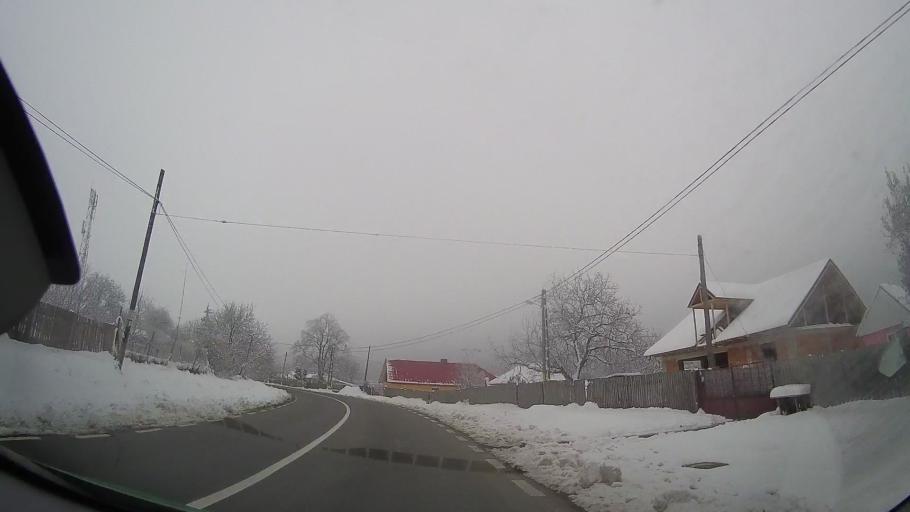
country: RO
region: Neamt
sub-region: Comuna Poenari
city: Poienari
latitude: 46.8792
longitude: 27.1322
